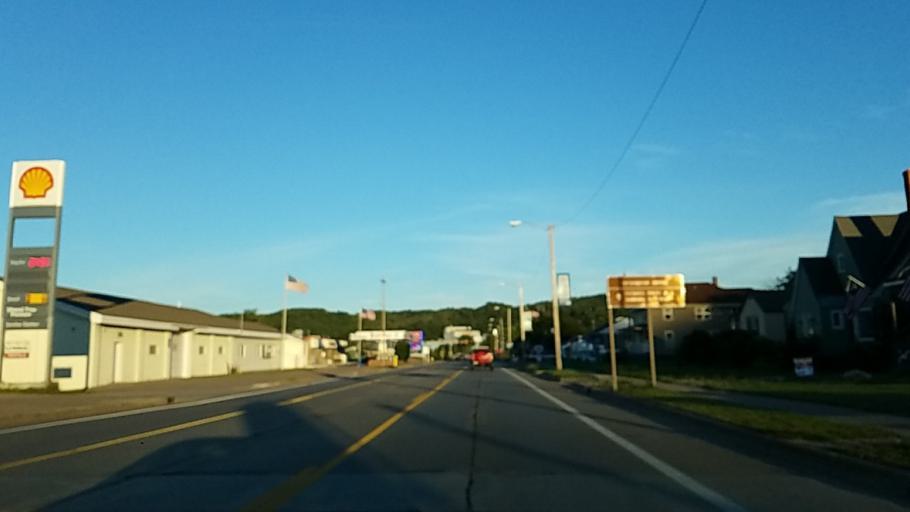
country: US
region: Michigan
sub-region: Alger County
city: Munising
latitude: 46.4107
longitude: -86.6529
